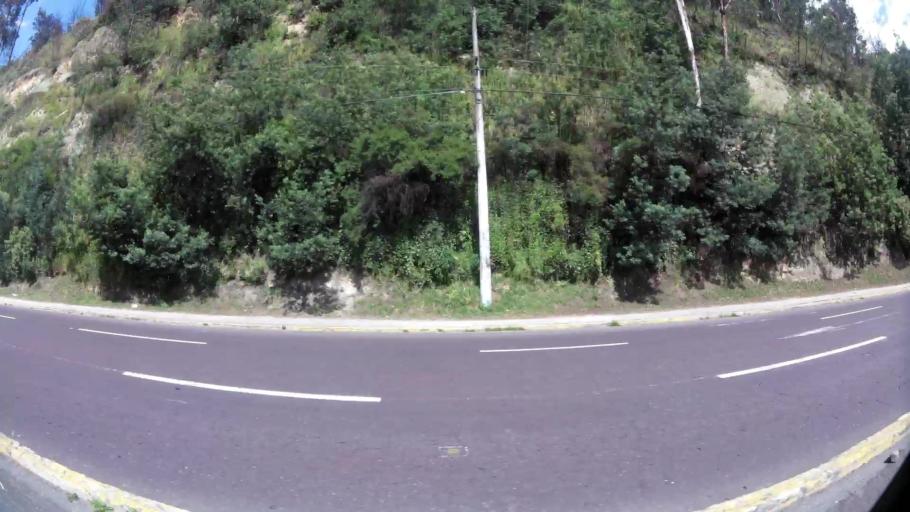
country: EC
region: Pichincha
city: Quito
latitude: -0.0974
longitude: -78.4690
